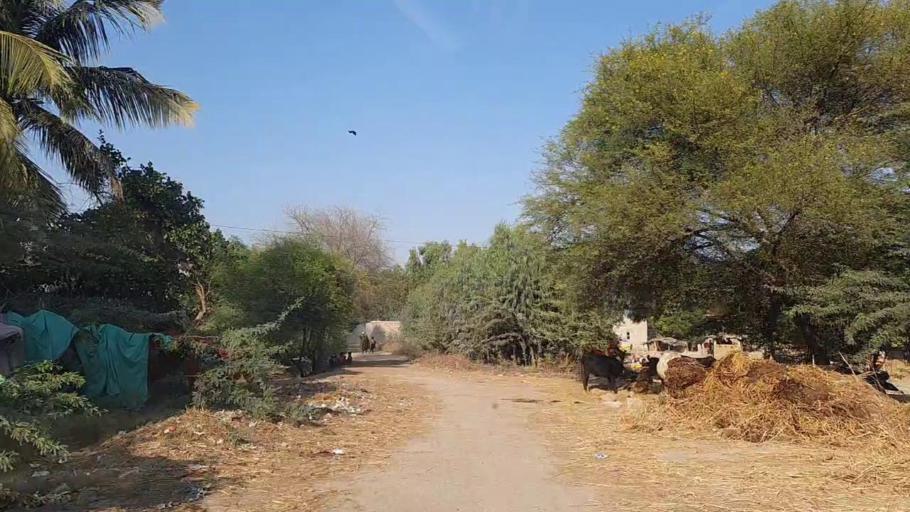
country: PK
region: Sindh
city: Thatta
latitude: 24.7676
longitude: 67.9668
